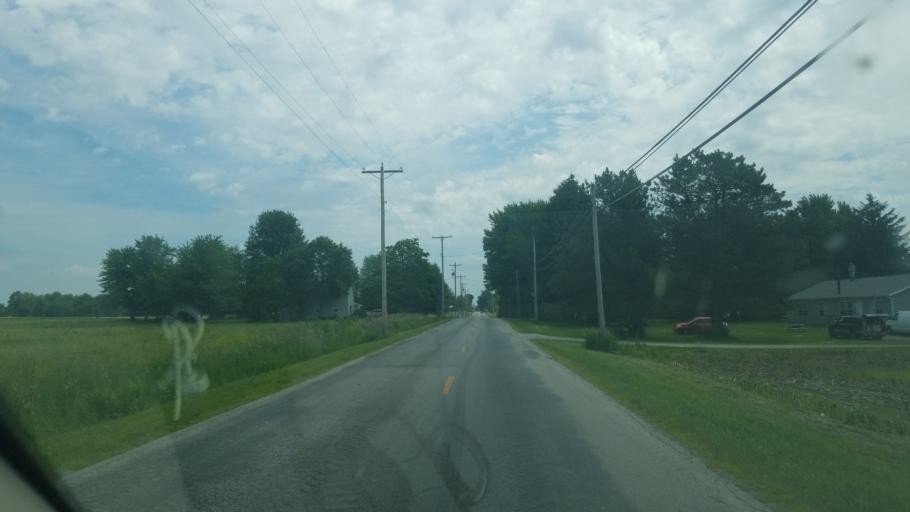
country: US
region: Ohio
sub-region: Wood County
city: Bowling Green
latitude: 41.2975
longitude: -83.6580
